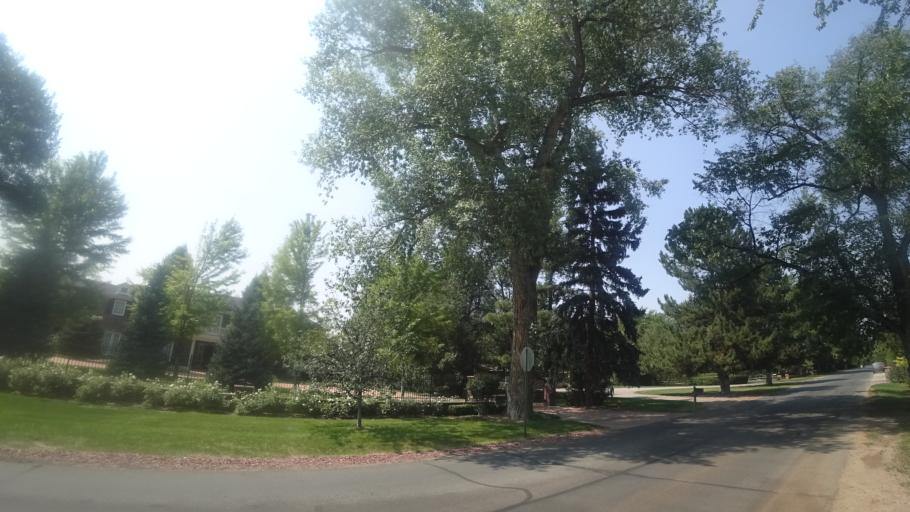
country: US
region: Colorado
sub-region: Arapahoe County
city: Cherry Hills Village
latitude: 39.6263
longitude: -104.9691
